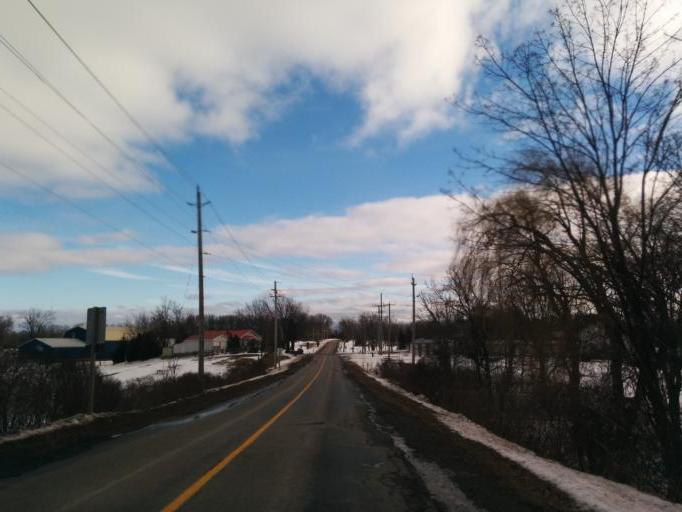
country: CA
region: Ontario
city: Ancaster
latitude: 42.9485
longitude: -79.8706
